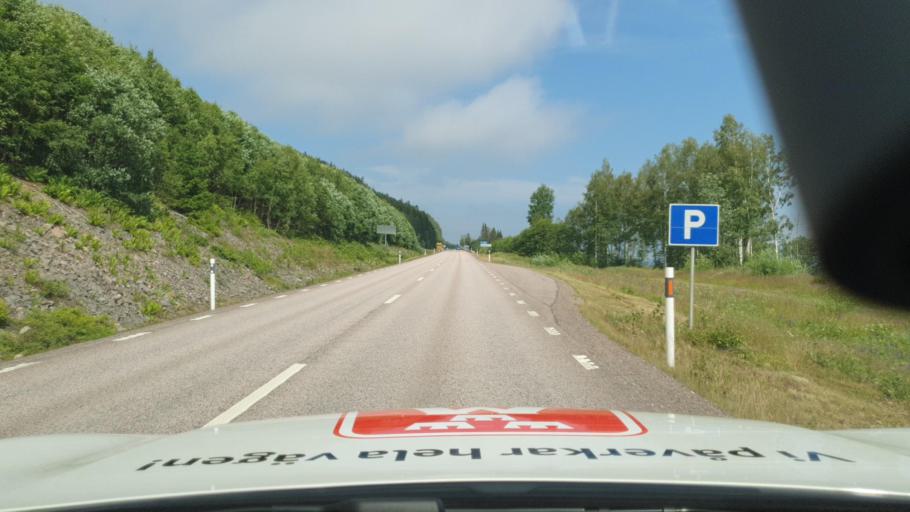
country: SE
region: Vaermland
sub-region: Sunne Kommun
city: Sunne
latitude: 59.9780
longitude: 13.1032
